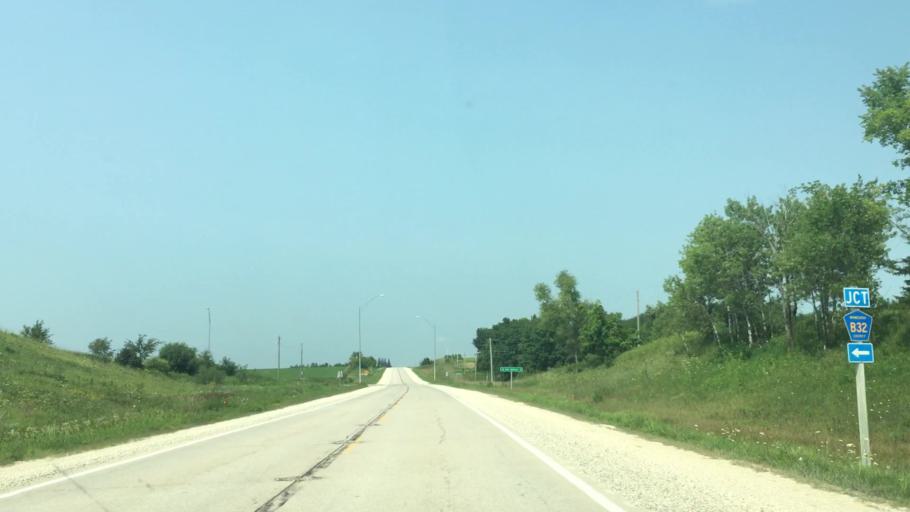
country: US
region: Iowa
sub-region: Fayette County
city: West Union
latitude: 43.1277
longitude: -91.8692
